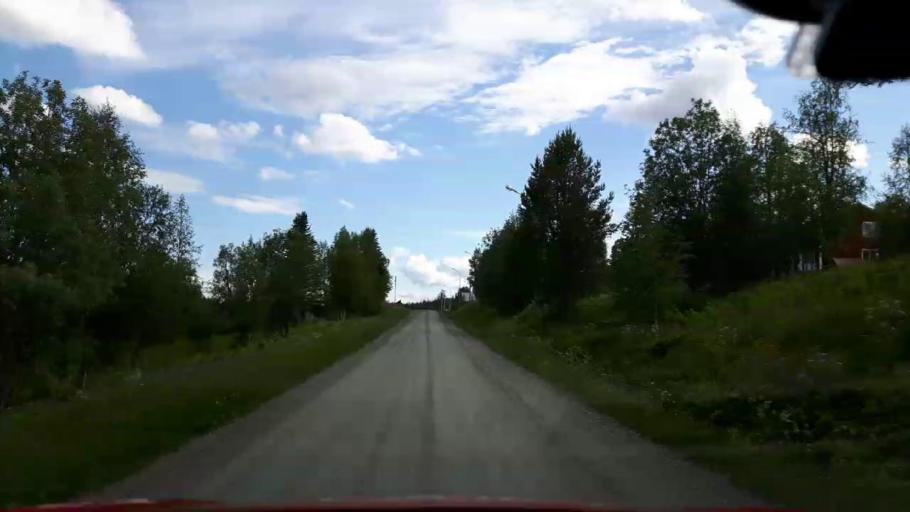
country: SE
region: Jaemtland
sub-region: Krokoms Kommun
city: Valla
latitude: 63.8307
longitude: 14.0403
